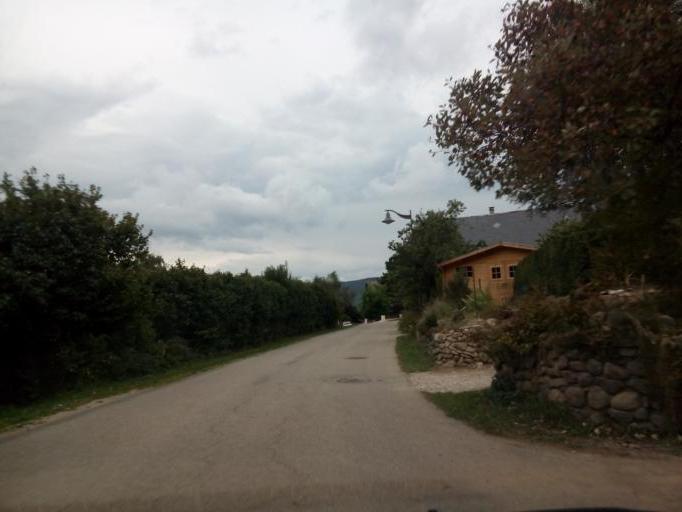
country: FR
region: Rhone-Alpes
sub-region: Departement de l'Isere
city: Pierre-Chatel
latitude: 44.9533
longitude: 5.8085
